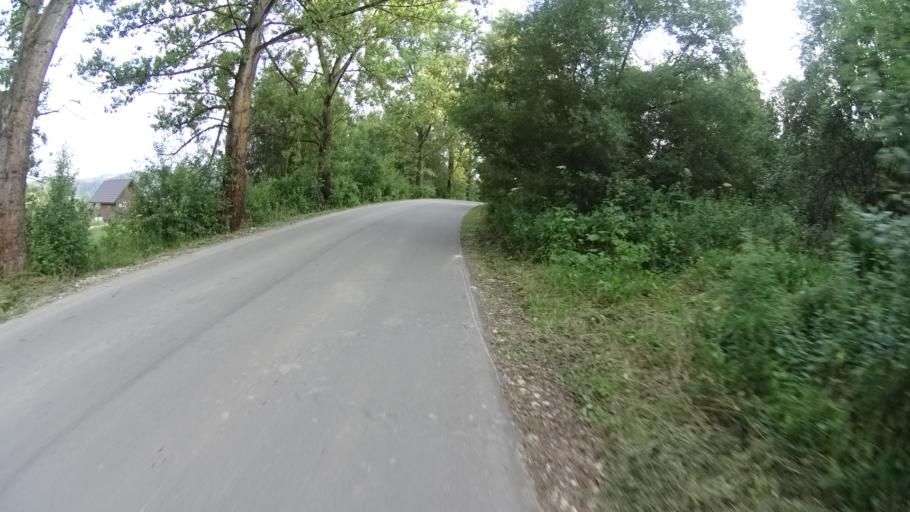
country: PL
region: Lesser Poland Voivodeship
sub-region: Powiat nowotarski
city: Maniowy
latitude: 49.4497
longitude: 20.2793
